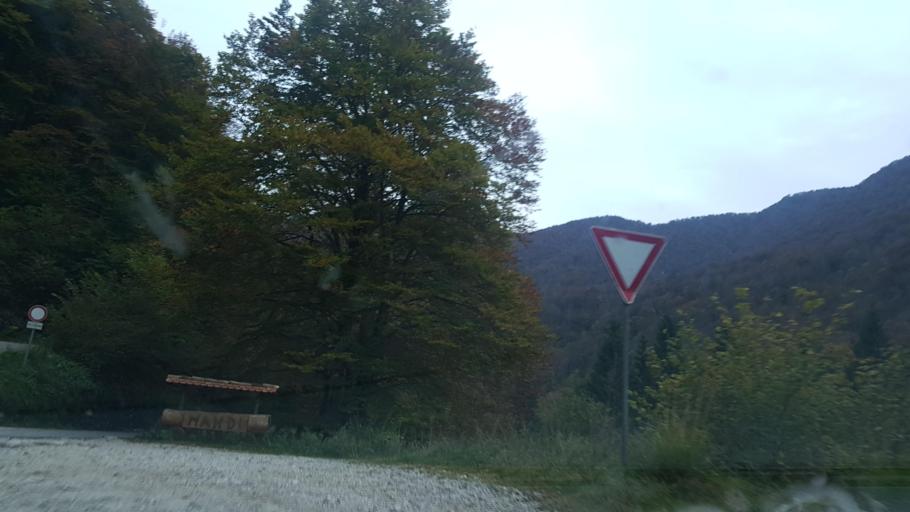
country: IT
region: Friuli Venezia Giulia
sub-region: Provincia di Udine
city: Preone
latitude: 46.3439
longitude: 12.8824
